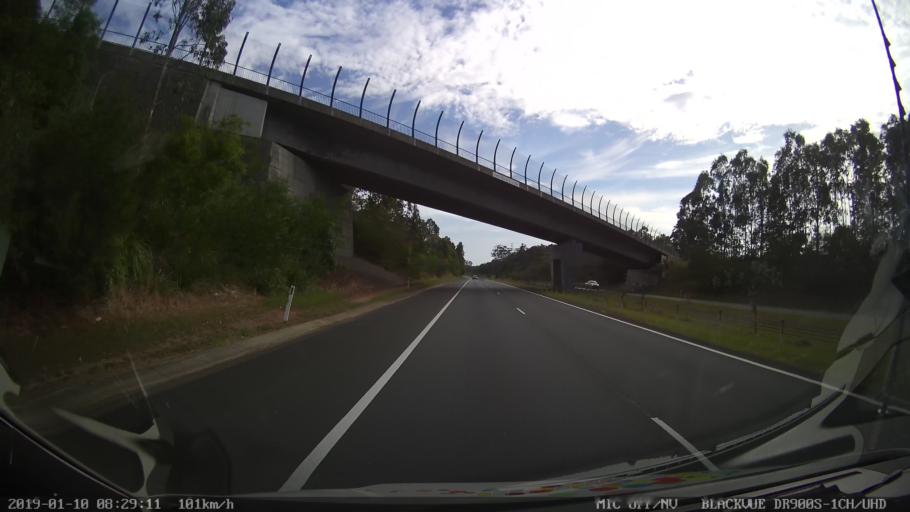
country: AU
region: New South Wales
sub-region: Coffs Harbour
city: Bonville
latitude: -30.3857
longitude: 153.0423
